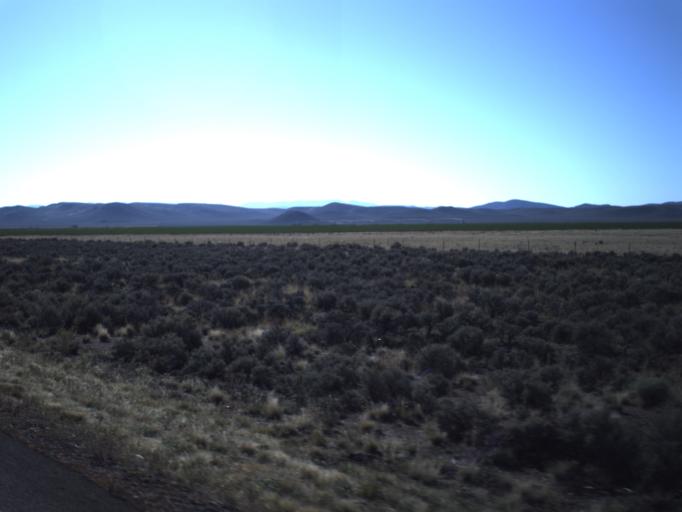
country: US
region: Utah
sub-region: Washington County
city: Enterprise
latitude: 37.7639
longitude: -113.8101
